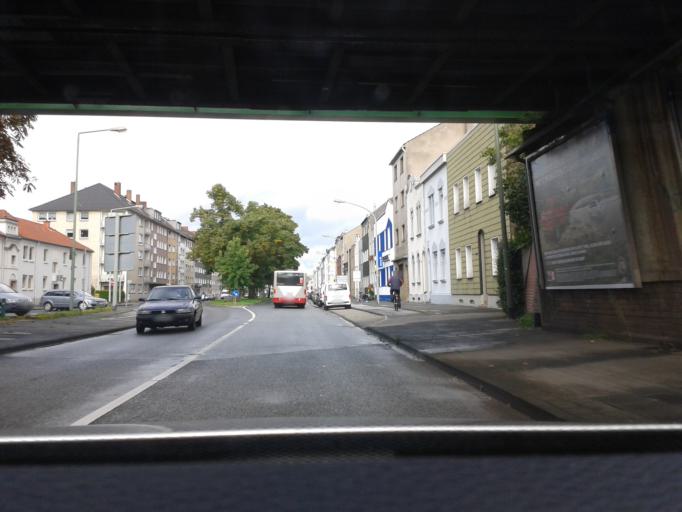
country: DE
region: North Rhine-Westphalia
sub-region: Regierungsbezirk Dusseldorf
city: Duisburg
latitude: 51.4158
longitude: 6.7925
